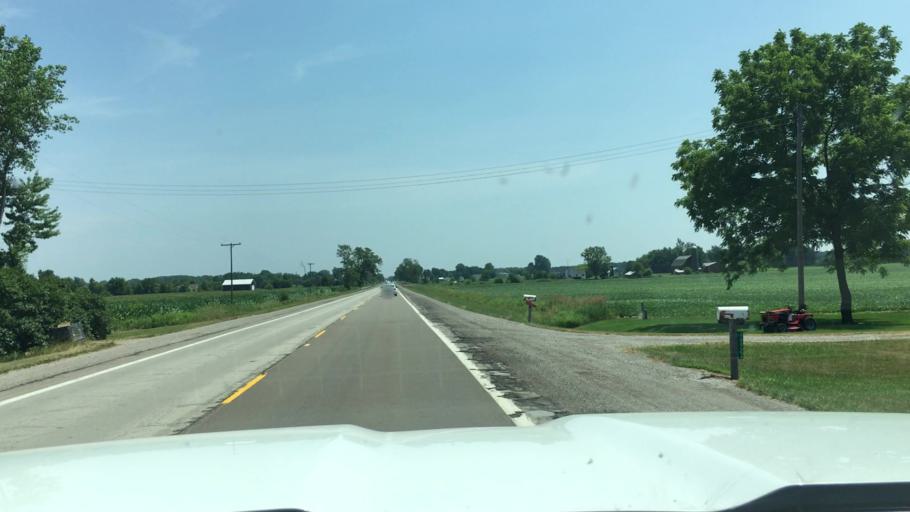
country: US
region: Michigan
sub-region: Saginaw County
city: Chesaning
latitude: 43.1869
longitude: -84.2467
